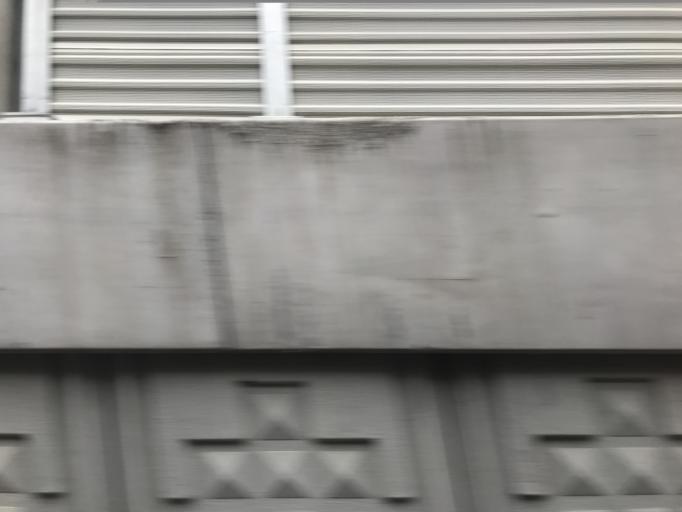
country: TR
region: Istanbul
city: guengoeren merter
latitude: 40.9817
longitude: 28.8798
